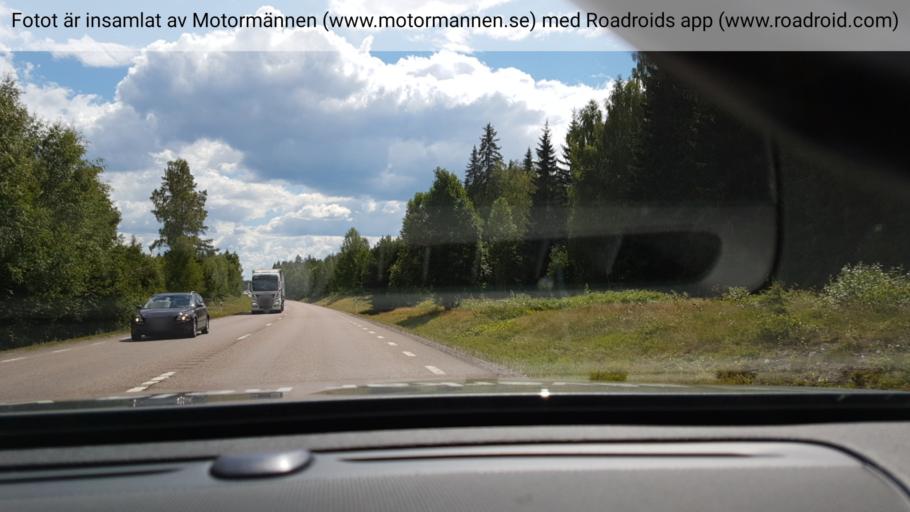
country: SE
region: Dalarna
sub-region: Faluns Kommun
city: Falun
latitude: 60.6429
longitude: 15.5746
